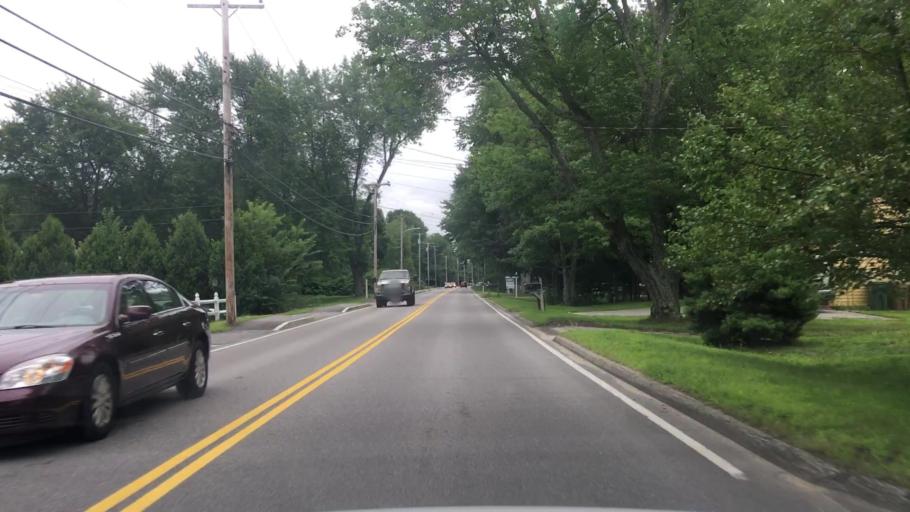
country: US
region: Maine
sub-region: York County
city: Biddeford
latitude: 43.5098
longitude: -70.4621
